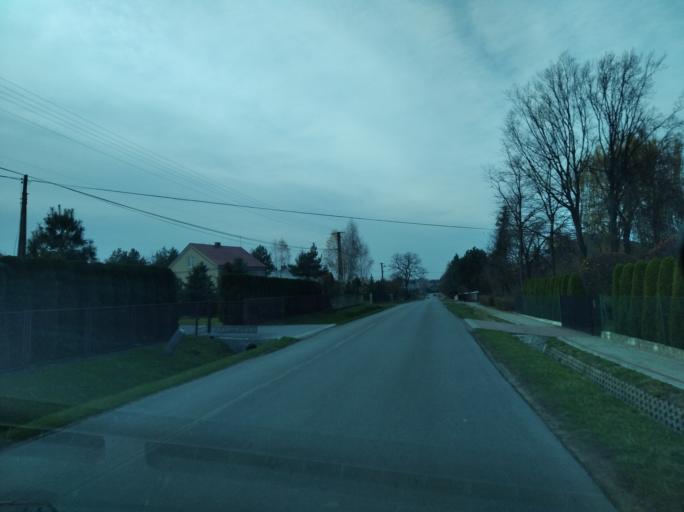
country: PL
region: Subcarpathian Voivodeship
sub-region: Powiat ropczycko-sedziszowski
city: Iwierzyce
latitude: 50.0546
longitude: 21.7426
